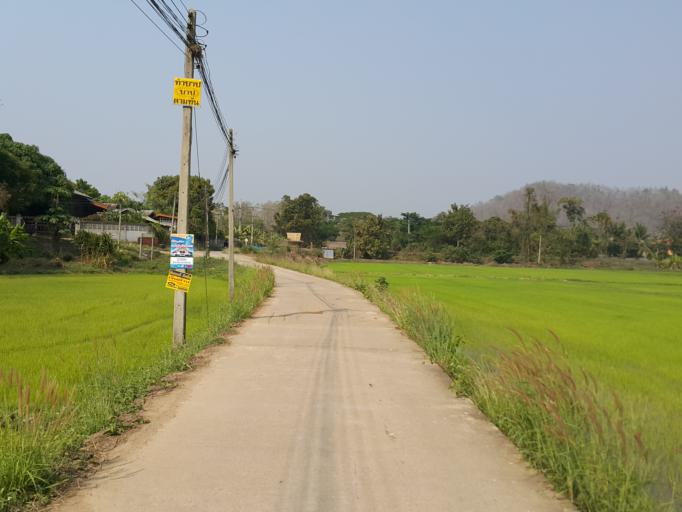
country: TH
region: Sukhothai
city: Thung Saliam
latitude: 17.3300
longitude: 99.5293
